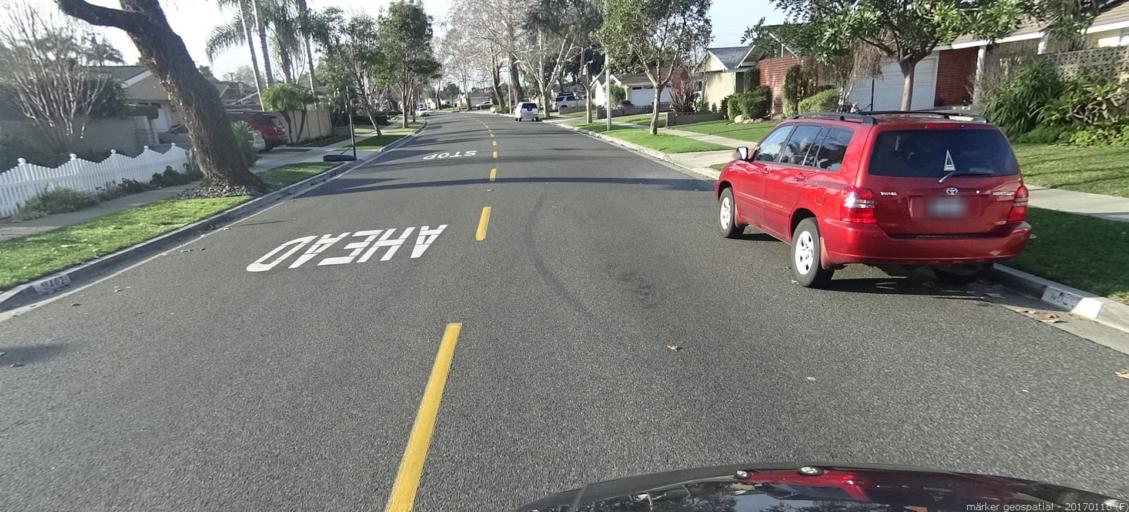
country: US
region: California
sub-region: Orange County
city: Rossmoor
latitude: 33.7980
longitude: -118.0847
